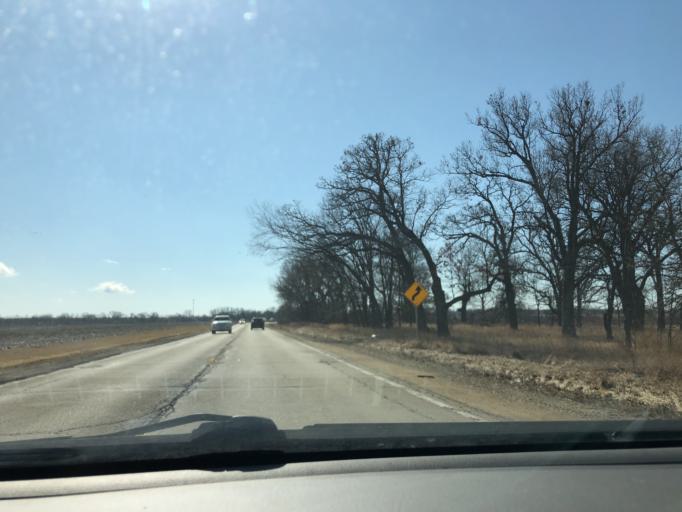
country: US
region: Illinois
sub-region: Kane County
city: Pingree Grove
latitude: 42.0981
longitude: -88.4545
